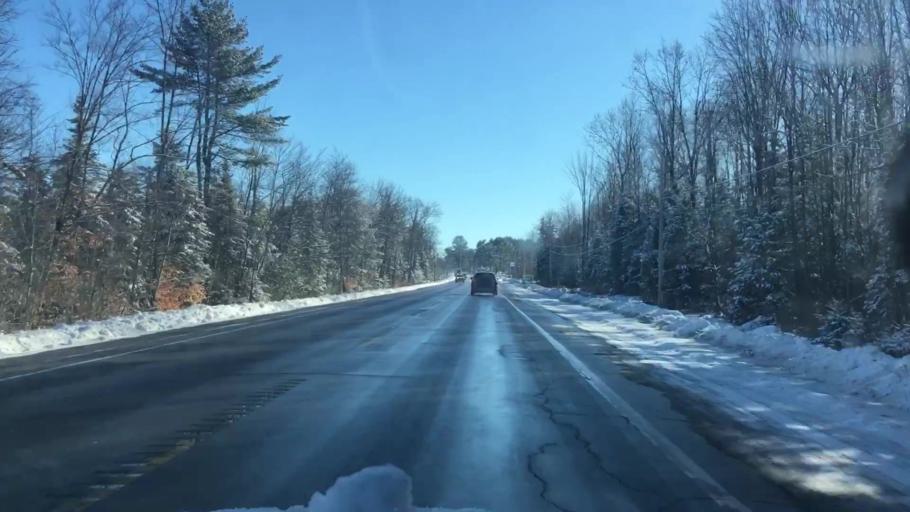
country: US
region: Maine
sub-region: Cumberland County
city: Bridgton
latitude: 44.0280
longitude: -70.6935
